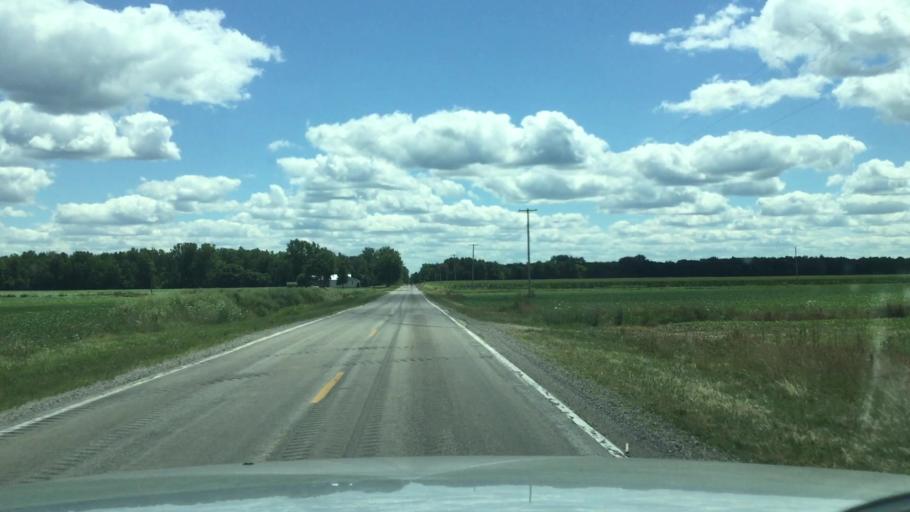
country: US
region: Michigan
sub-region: Saginaw County
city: Saint Charles
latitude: 43.3366
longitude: -84.1898
